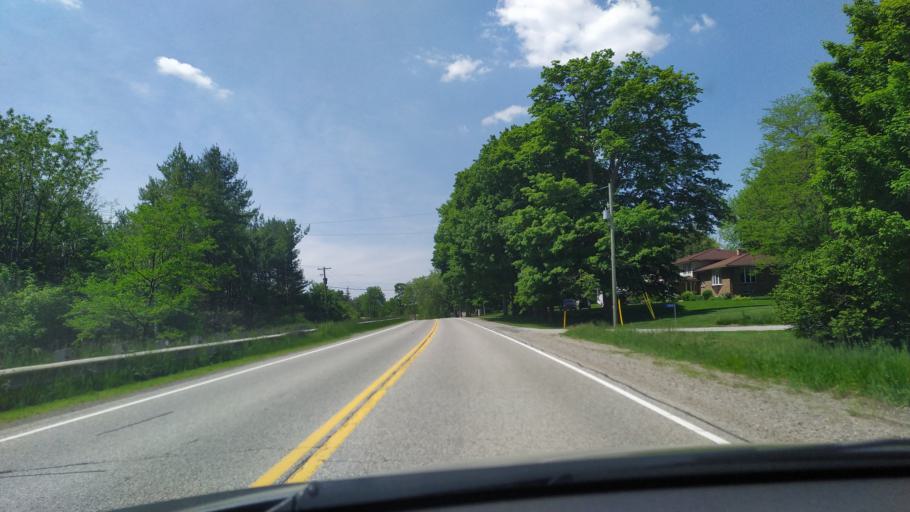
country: CA
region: Ontario
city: Dorchester
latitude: 43.0760
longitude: -81.0042
